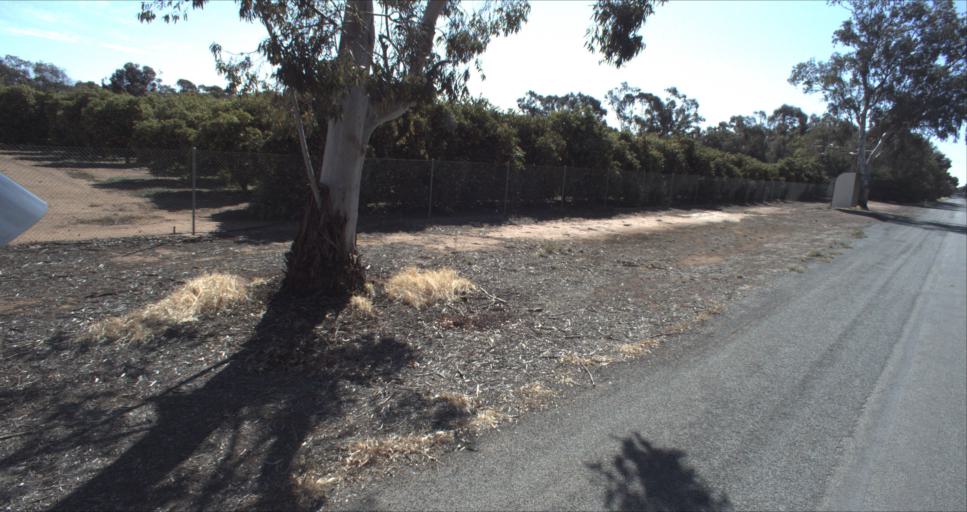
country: AU
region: New South Wales
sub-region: Leeton
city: Leeton
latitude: -34.5582
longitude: 146.3878
